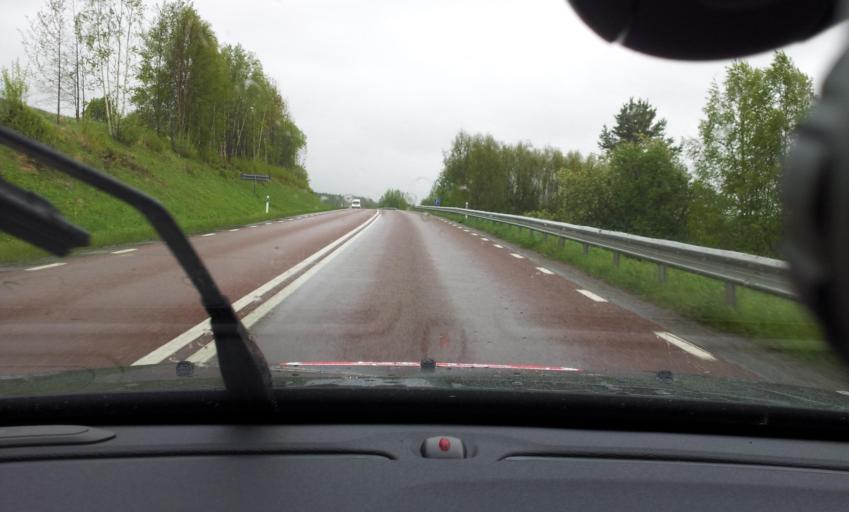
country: SE
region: Jaemtland
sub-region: Bergs Kommun
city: Hoverberg
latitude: 62.7647
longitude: 14.4381
